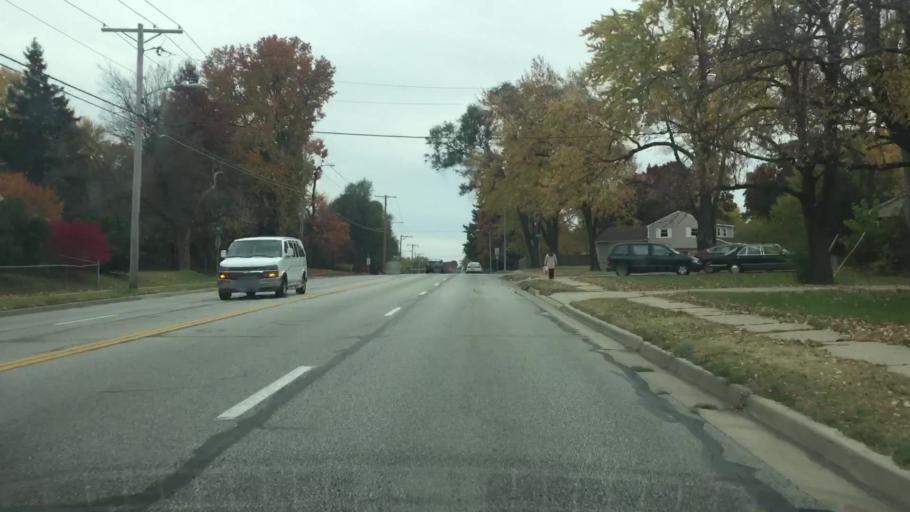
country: US
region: Kansas
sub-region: Johnson County
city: Merriam
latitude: 39.0025
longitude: -94.7239
